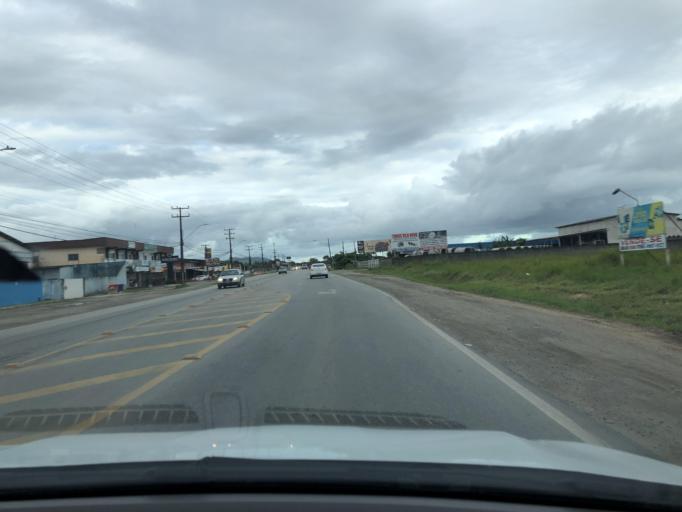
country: BR
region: Santa Catarina
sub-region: Joinville
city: Joinville
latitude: -26.3777
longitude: -48.7200
